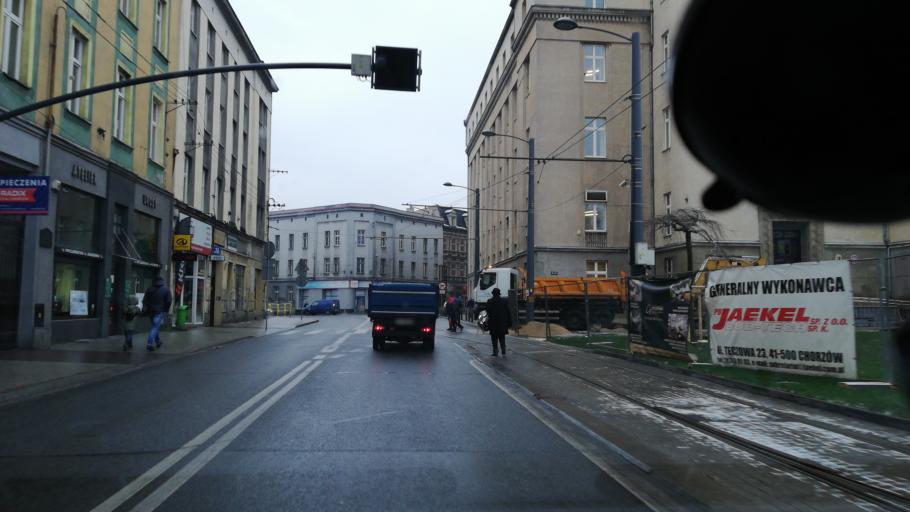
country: PL
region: Silesian Voivodeship
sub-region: Chorzow
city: Chorzow
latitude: 50.2974
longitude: 18.9541
